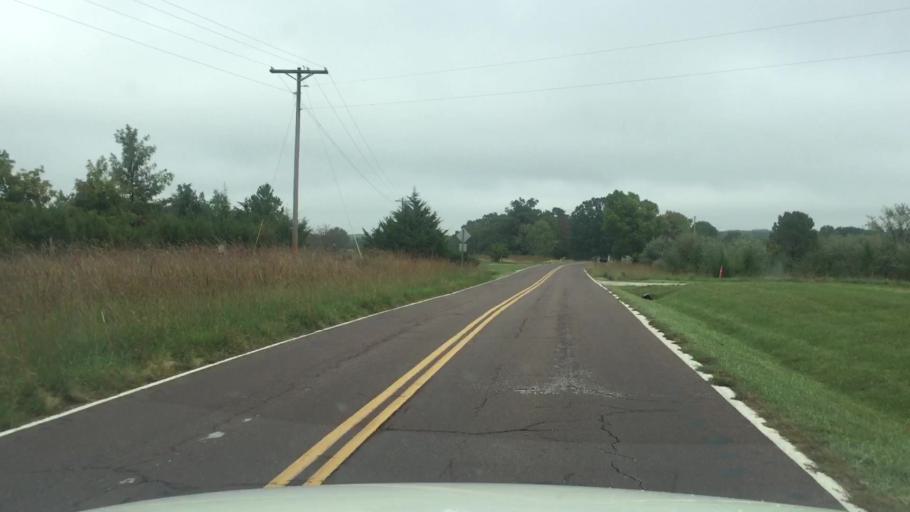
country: US
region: Missouri
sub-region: Boone County
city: Columbia
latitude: 38.8490
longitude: -92.3349
